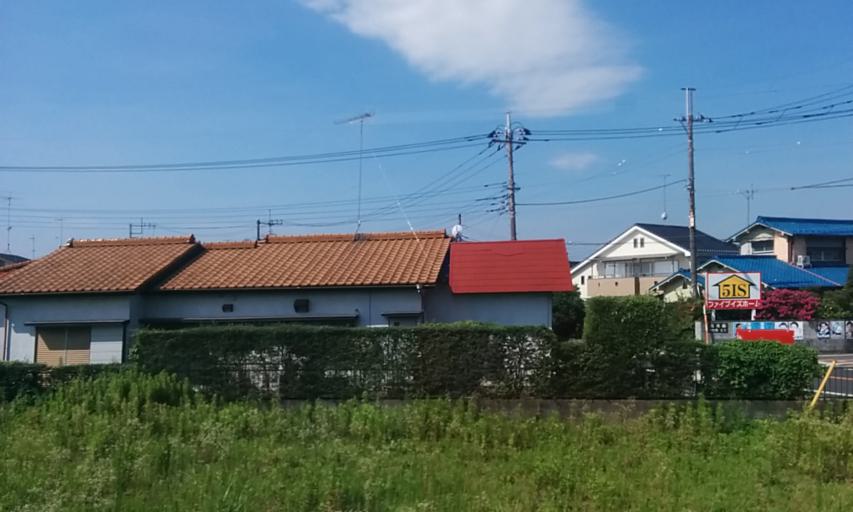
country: JP
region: Saitama
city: Kazo
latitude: 36.1315
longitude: 139.5829
